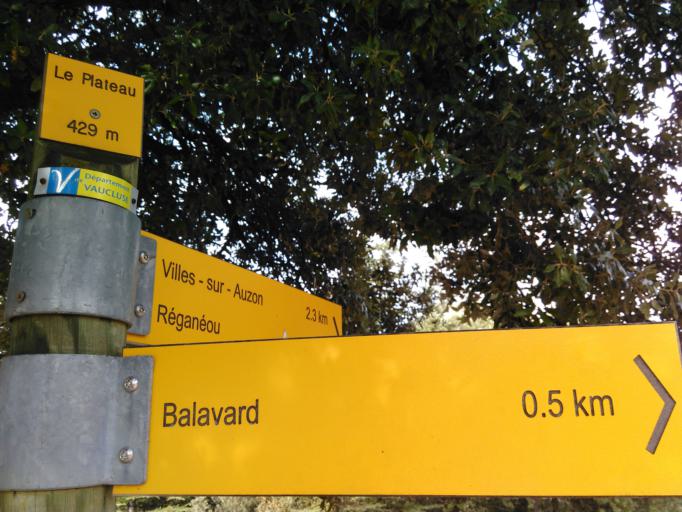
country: FR
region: Provence-Alpes-Cote d'Azur
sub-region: Departement du Vaucluse
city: Villes-sur-Auzon
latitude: 44.0399
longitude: 5.2467
